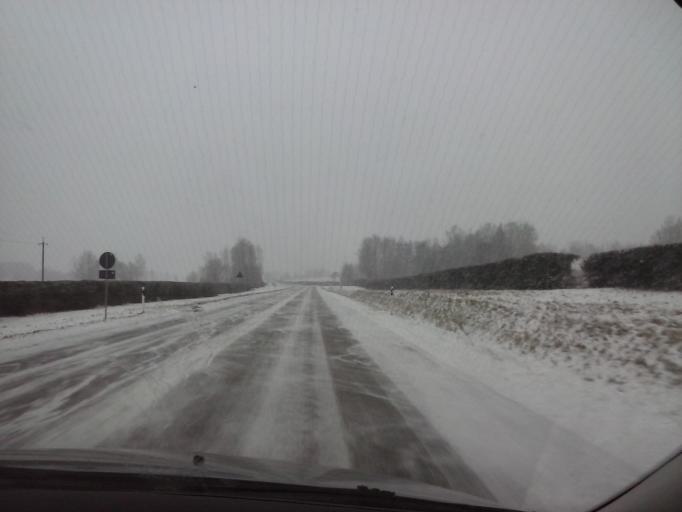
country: EE
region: Valgamaa
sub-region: Torva linn
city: Torva
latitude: 58.0442
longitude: 26.1907
